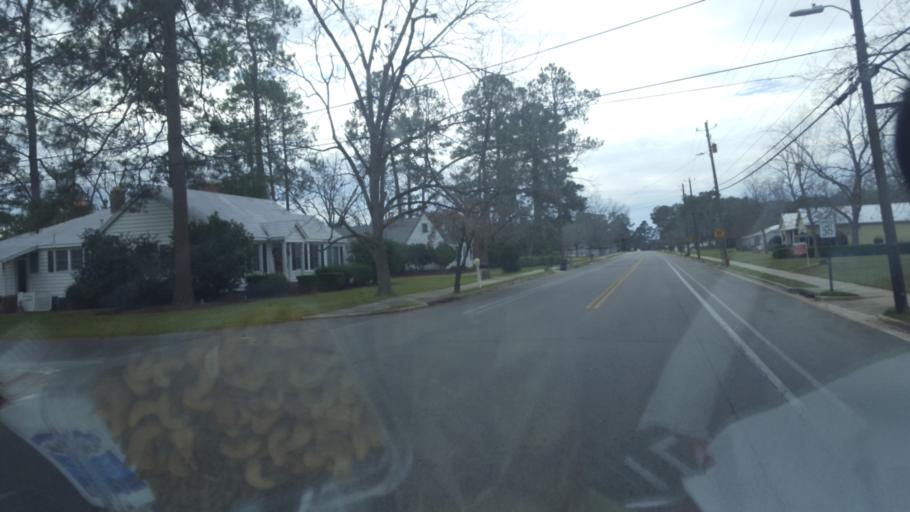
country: US
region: Georgia
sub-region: Berrien County
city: Nashville
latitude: 31.2014
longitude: -83.2561
